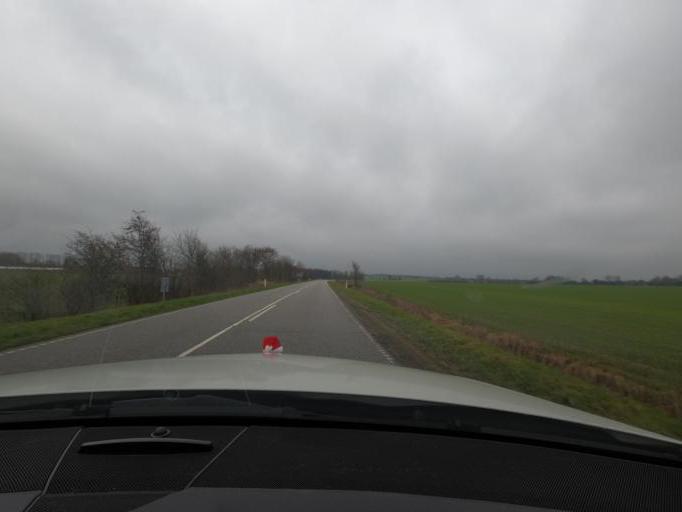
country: DK
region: South Denmark
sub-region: Haderslev Kommune
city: Starup
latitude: 55.2543
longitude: 9.6864
